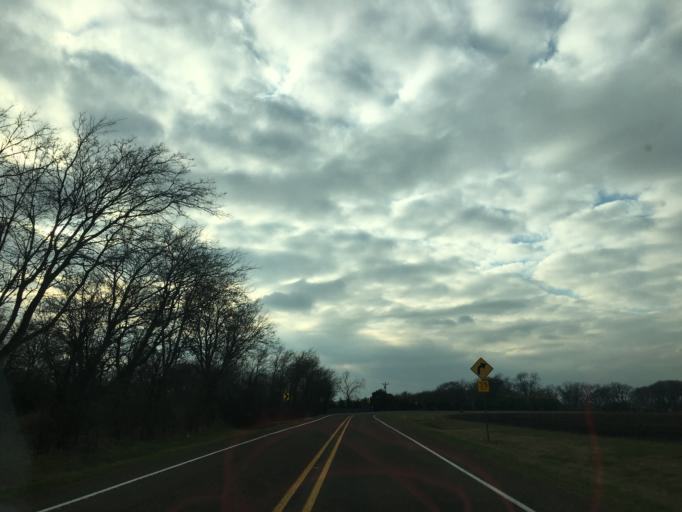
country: US
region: Texas
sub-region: Ellis County
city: Palmer
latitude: 32.4476
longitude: -96.7172
